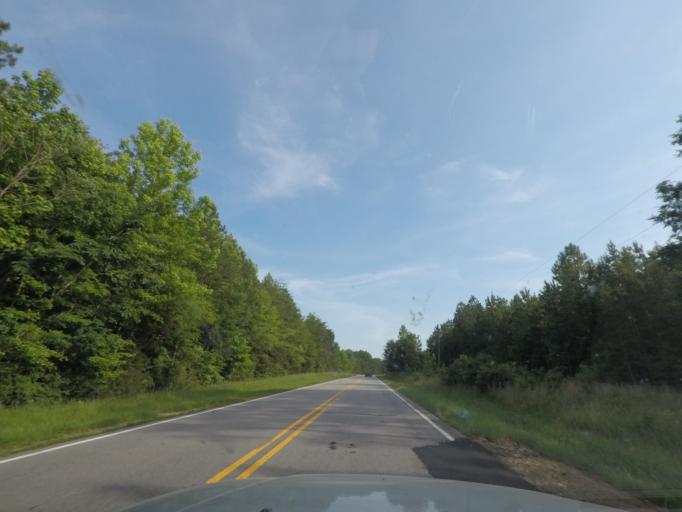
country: US
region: Virginia
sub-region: Mecklenburg County
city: Clarksville
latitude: 36.5181
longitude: -78.5341
